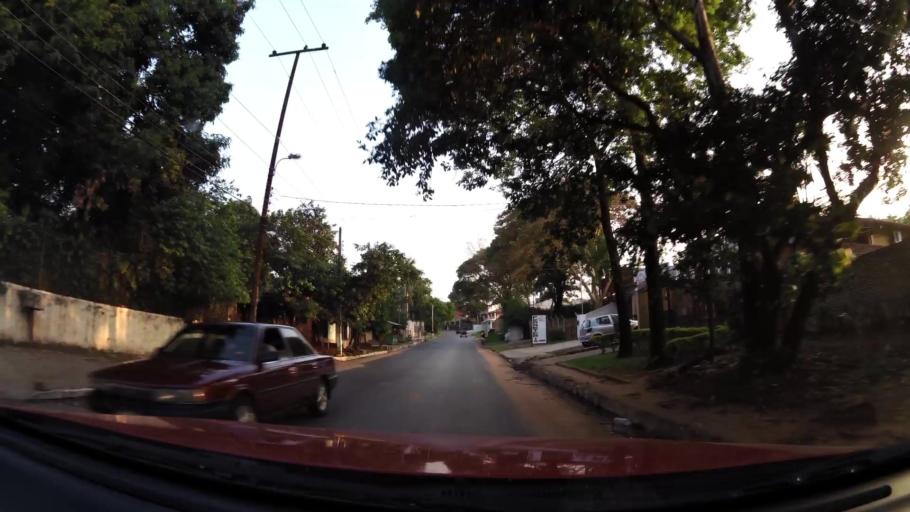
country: PY
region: Central
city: Lambare
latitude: -25.3525
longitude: -57.6004
